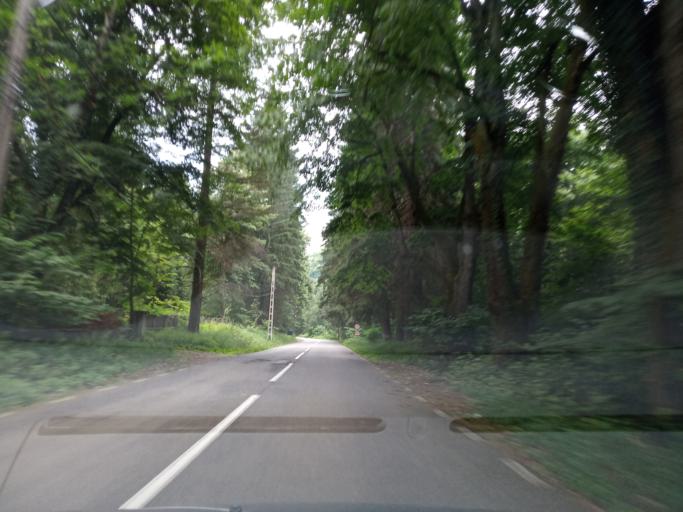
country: RO
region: Gorj
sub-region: Comuna Tismana
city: Pocruia
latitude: 45.0743
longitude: 22.9319
